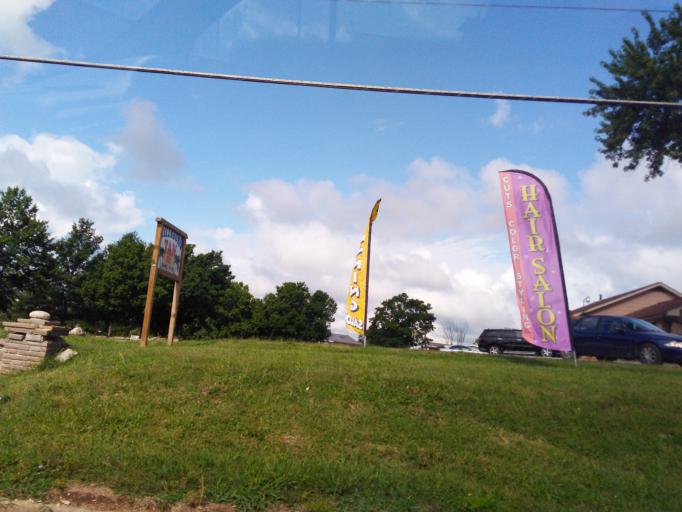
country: US
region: Missouri
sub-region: Jefferson County
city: Hillsboro
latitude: 38.2382
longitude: -90.5618
